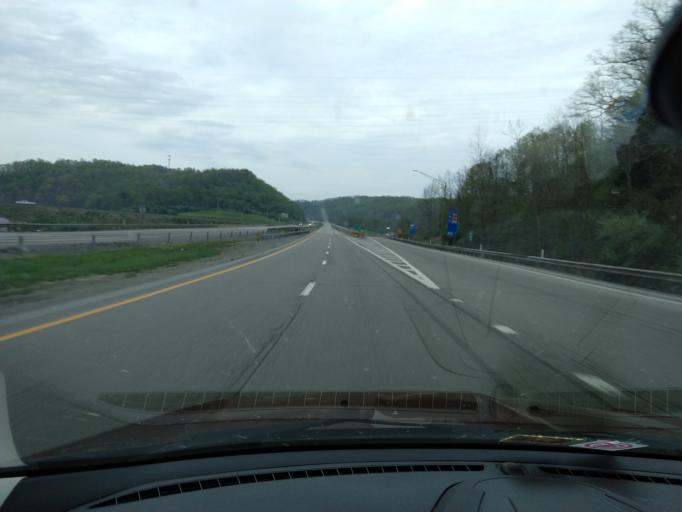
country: US
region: West Virginia
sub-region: Lewis County
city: Weston
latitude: 39.0182
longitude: -80.4301
